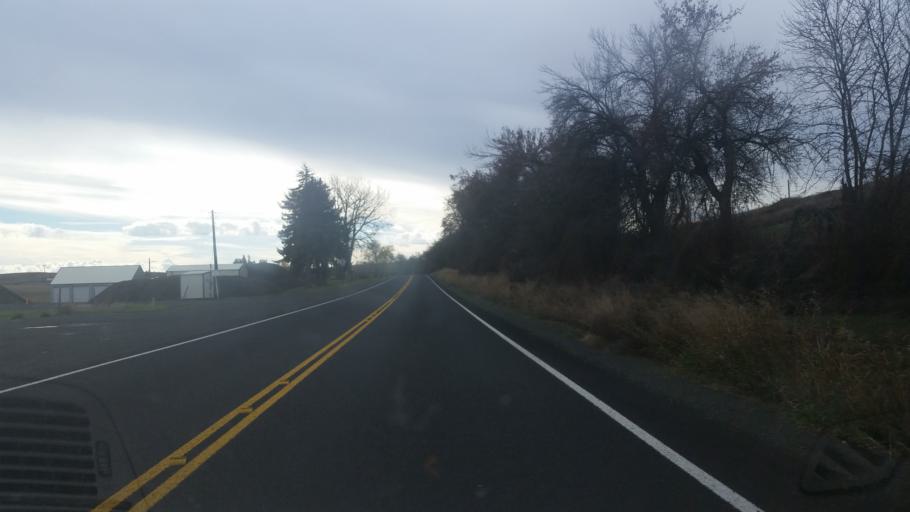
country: US
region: Washington
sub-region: Whitman County
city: Colfax
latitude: 47.2183
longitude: -117.3635
